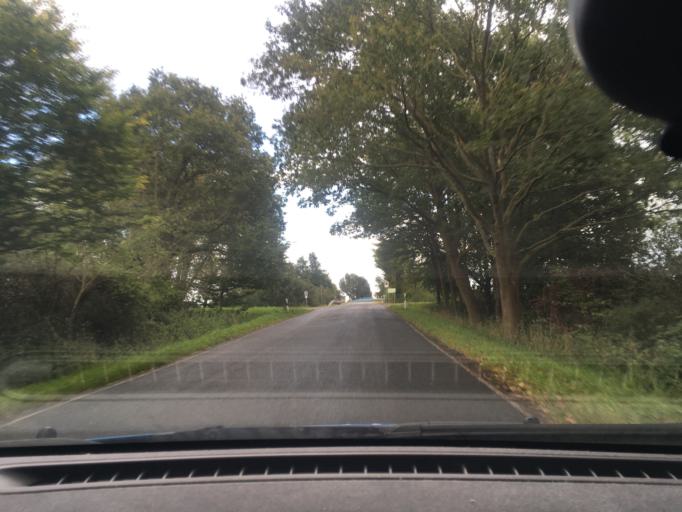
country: DE
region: Lower Saxony
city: Neu Darchau
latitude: 53.3311
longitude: 10.8785
